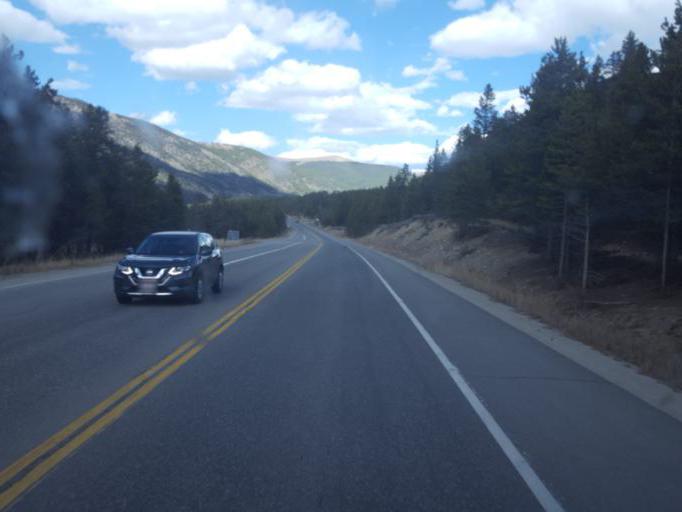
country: US
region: Colorado
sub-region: Lake County
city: Leadville North
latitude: 39.2735
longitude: -106.2859
